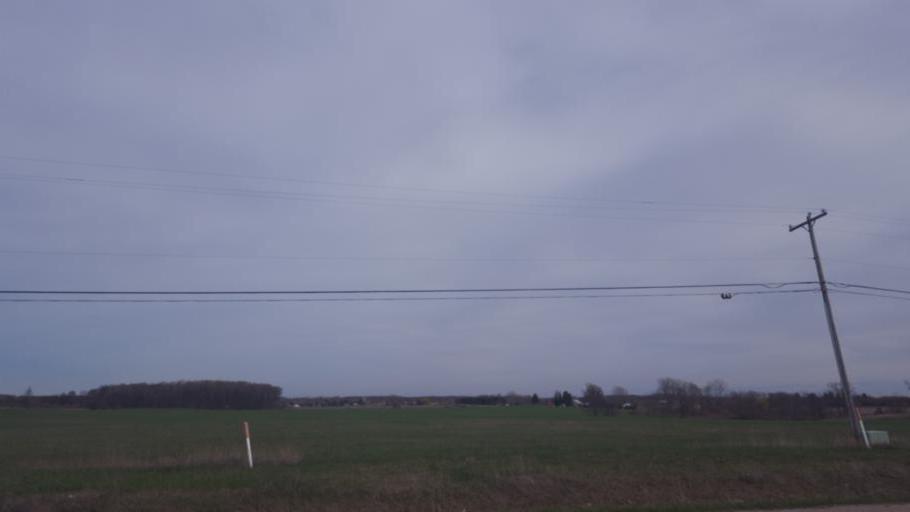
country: US
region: Michigan
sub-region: Clare County
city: Clare
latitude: 43.8606
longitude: -84.7681
